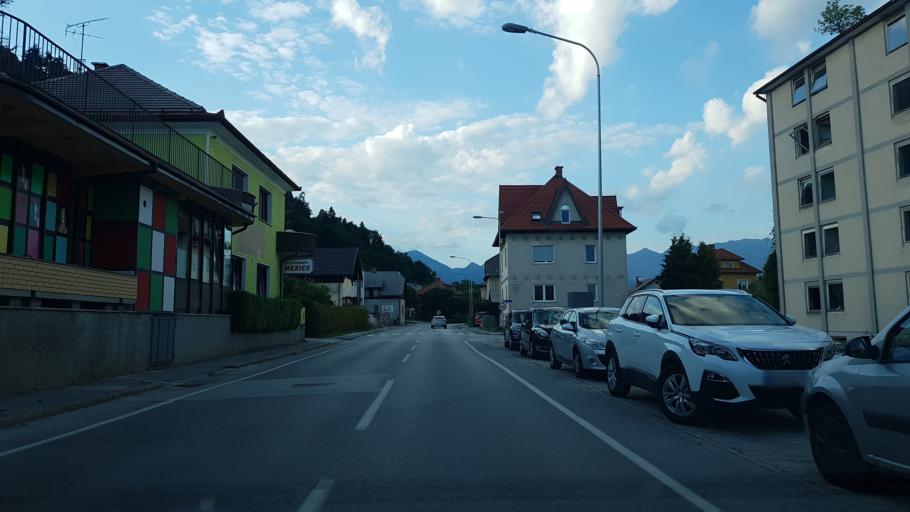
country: SI
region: Kranj
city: Kranj
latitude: 46.2356
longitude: 14.3452
